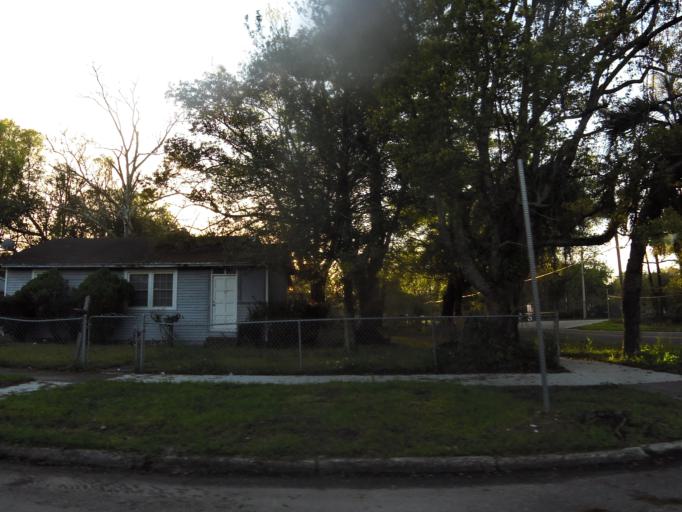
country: US
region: Florida
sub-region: Duval County
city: Jacksonville
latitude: 30.3401
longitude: -81.7122
